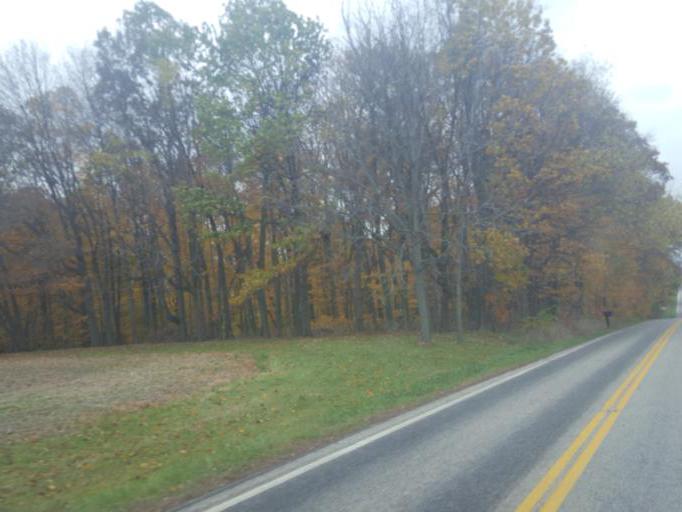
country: US
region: Ohio
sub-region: Ashland County
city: Loudonville
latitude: 40.7509
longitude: -82.2153
